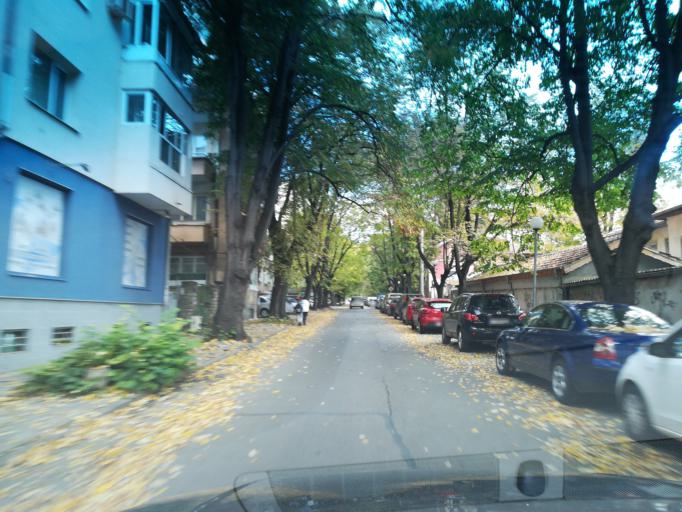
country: BG
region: Stara Zagora
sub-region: Obshtina Stara Zagora
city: Stara Zagora
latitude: 42.4303
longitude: 25.6281
